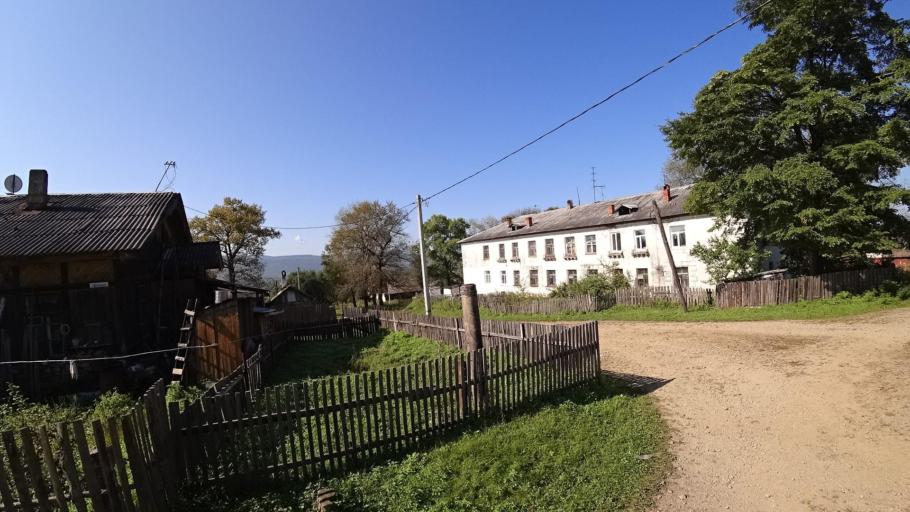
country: RU
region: Jewish Autonomous Oblast
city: Bira
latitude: 49.0025
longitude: 132.4682
